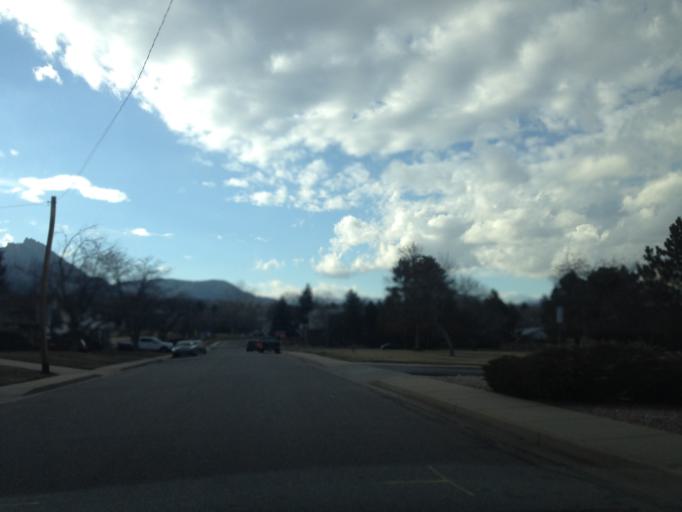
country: US
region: Colorado
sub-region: Boulder County
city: Boulder
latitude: 39.9810
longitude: -105.2540
